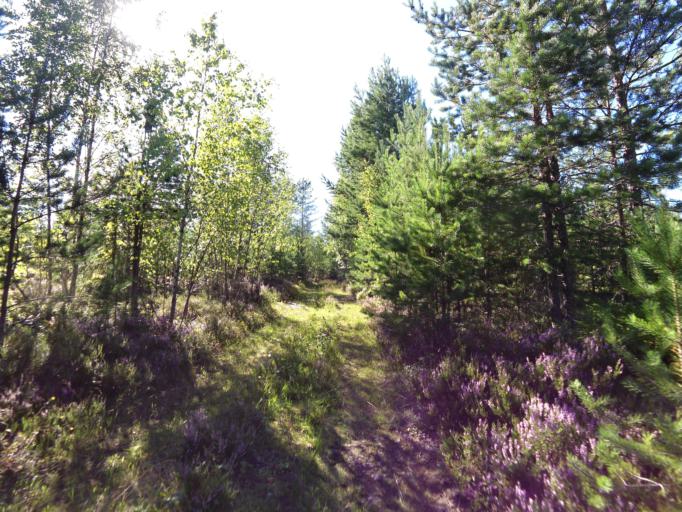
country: SE
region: Gaevleborg
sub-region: Sandvikens Kommun
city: Jarbo
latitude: 60.5636
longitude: 16.4831
